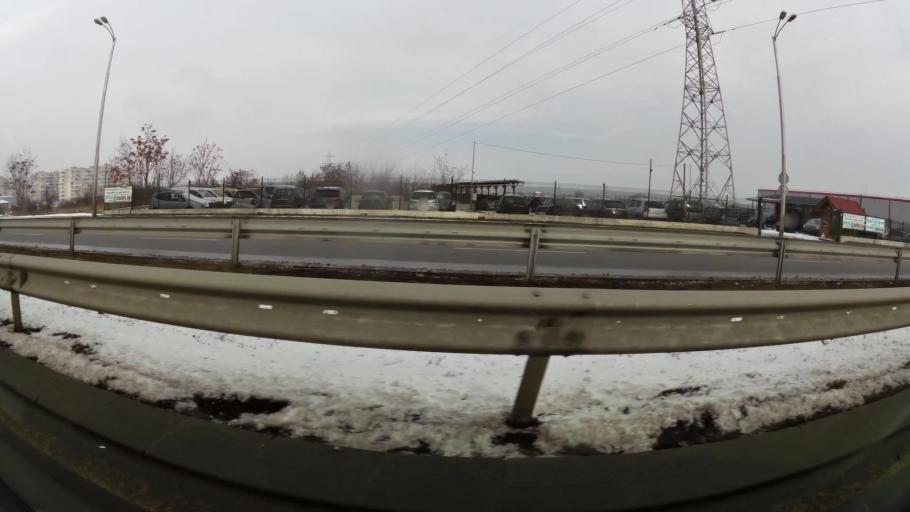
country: BG
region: Sofia-Capital
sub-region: Stolichna Obshtina
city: Sofia
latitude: 42.7097
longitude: 23.3925
